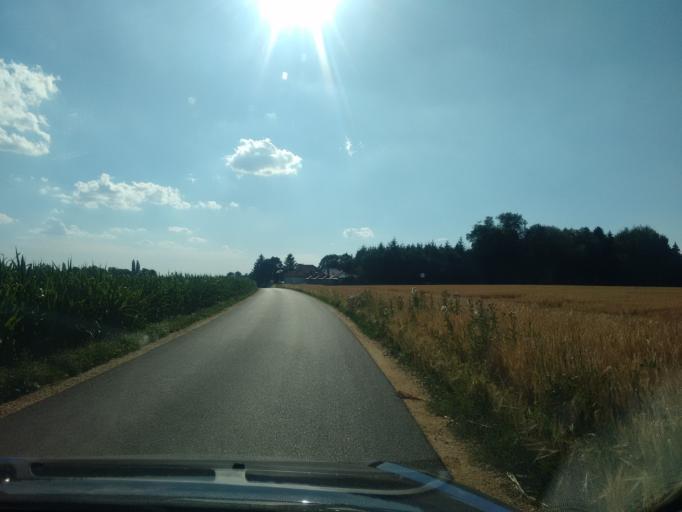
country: AT
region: Upper Austria
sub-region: Wels-Land
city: Thalheim bei Wels
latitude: 48.1337
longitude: 14.0328
